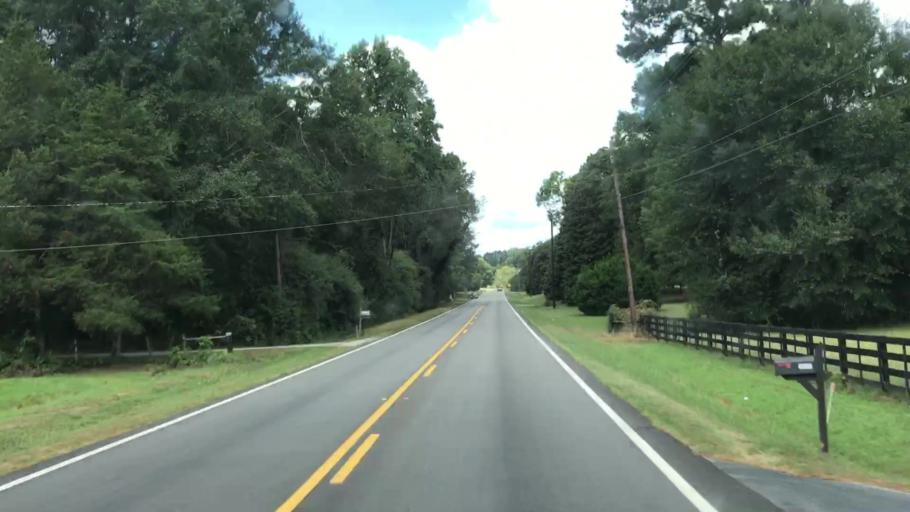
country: US
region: Georgia
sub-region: Greene County
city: Greensboro
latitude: 33.5628
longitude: -83.1427
